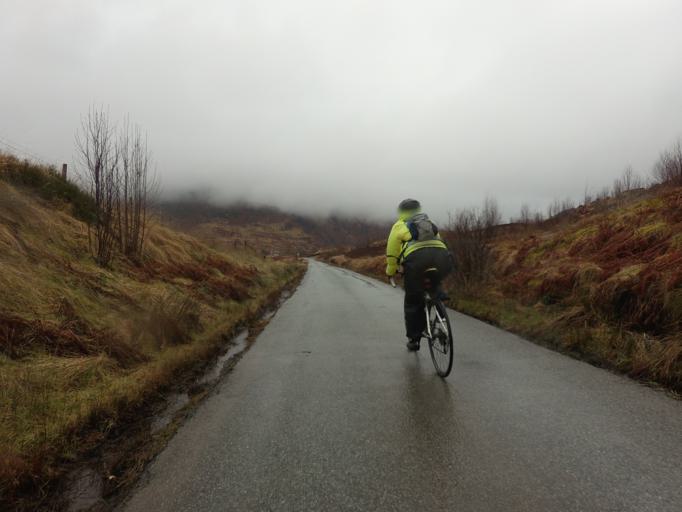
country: GB
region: Scotland
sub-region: West Dunbartonshire
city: Balloch
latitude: 56.2484
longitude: -4.5860
